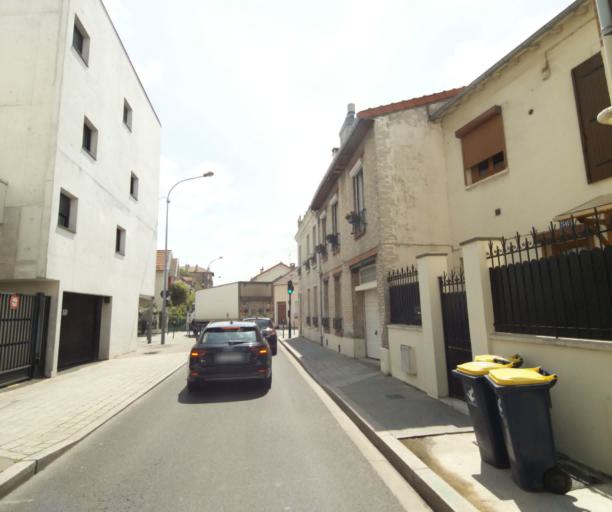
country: FR
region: Ile-de-France
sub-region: Departement des Hauts-de-Seine
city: La Garenne-Colombes
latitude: 48.9154
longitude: 2.2382
